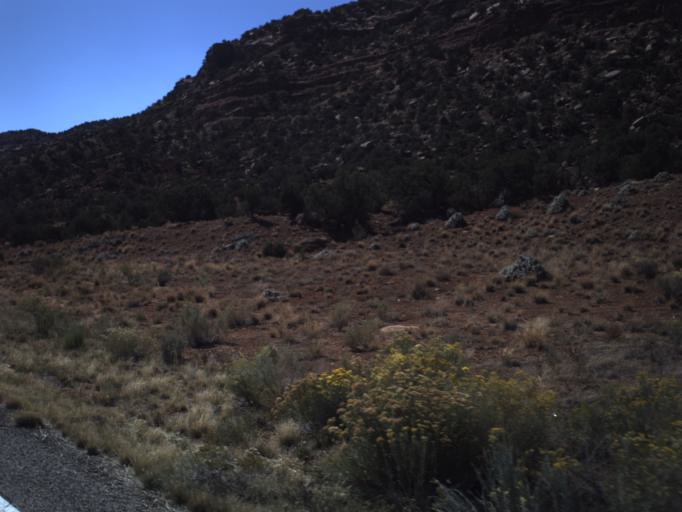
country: US
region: Utah
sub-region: San Juan County
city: Blanding
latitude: 37.6278
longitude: -110.0872
